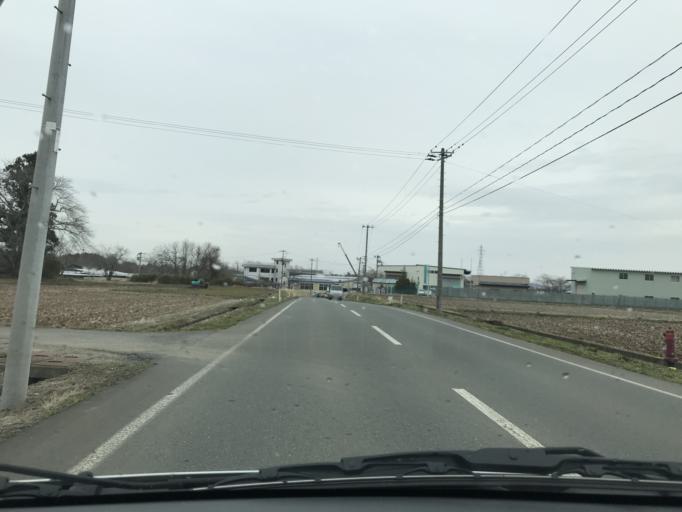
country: JP
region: Iwate
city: Mizusawa
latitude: 39.1766
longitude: 141.1134
